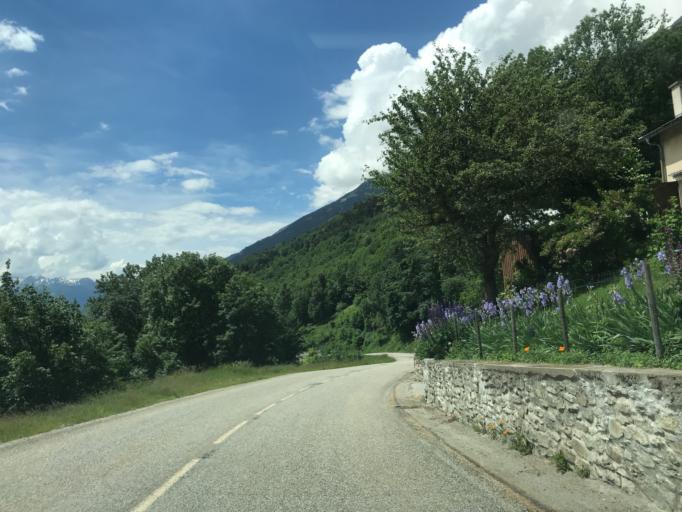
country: FR
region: Rhone-Alpes
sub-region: Departement de la Savoie
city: Modane
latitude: 45.2040
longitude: 6.6322
